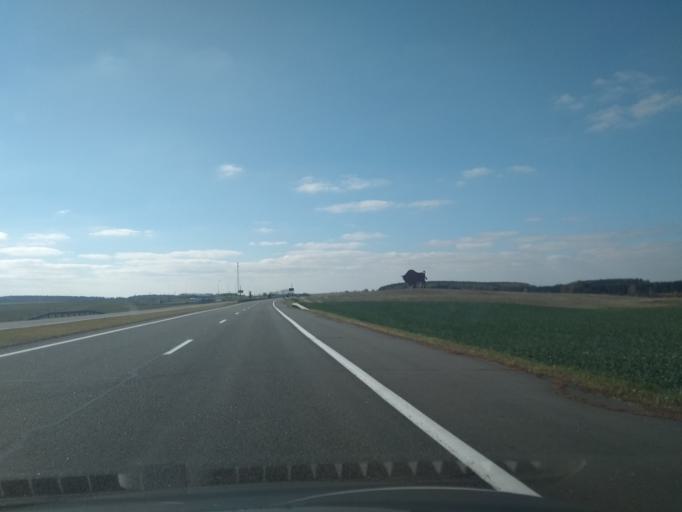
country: BY
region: Minsk
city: Snow
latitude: 53.3015
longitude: 26.3764
